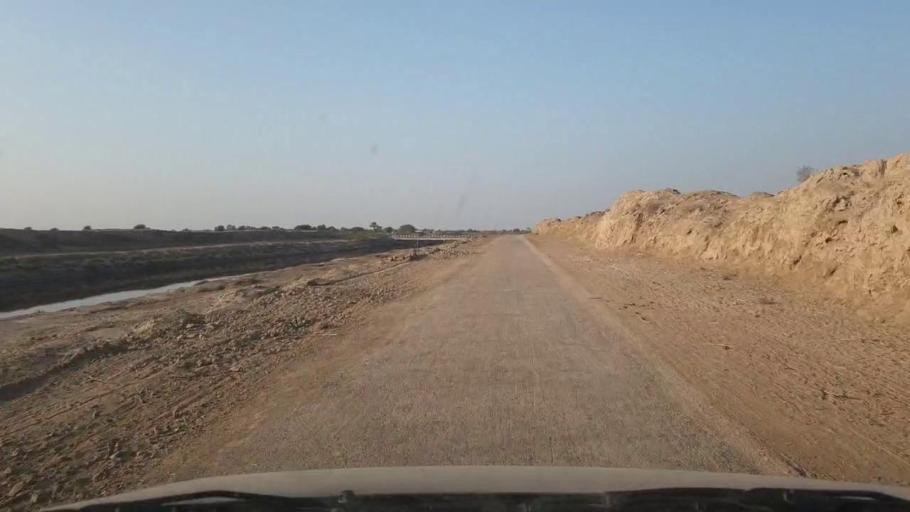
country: PK
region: Sindh
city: Samaro
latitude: 25.2958
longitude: 69.3311
